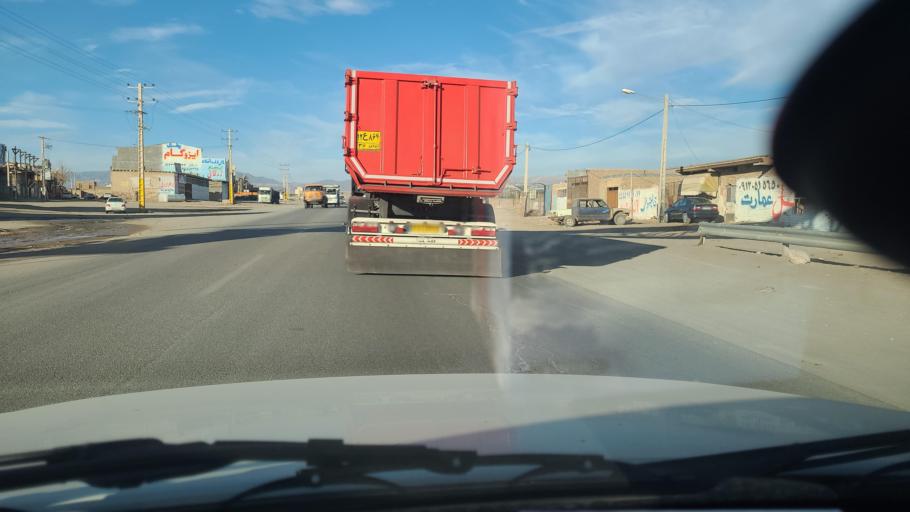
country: IR
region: Razavi Khorasan
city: Sabzevar
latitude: 36.2216
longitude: 57.6515
